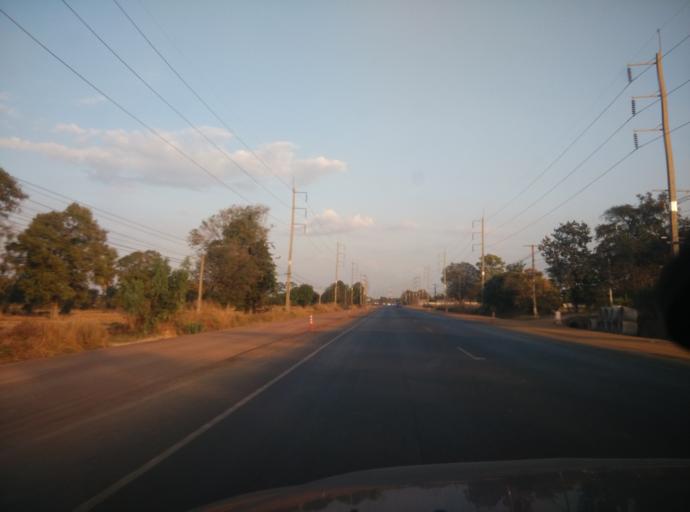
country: TH
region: Sisaket
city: Uthumphon Phisai
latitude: 15.1492
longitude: 104.2182
